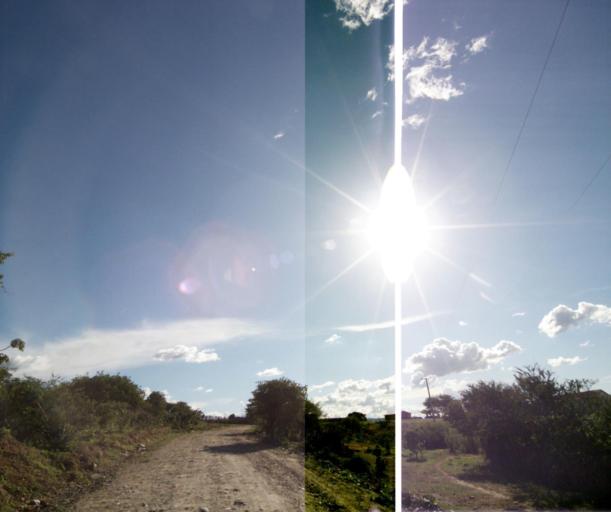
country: BR
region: Bahia
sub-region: Tanhacu
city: Tanhacu
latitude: -14.1827
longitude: -41.0116
